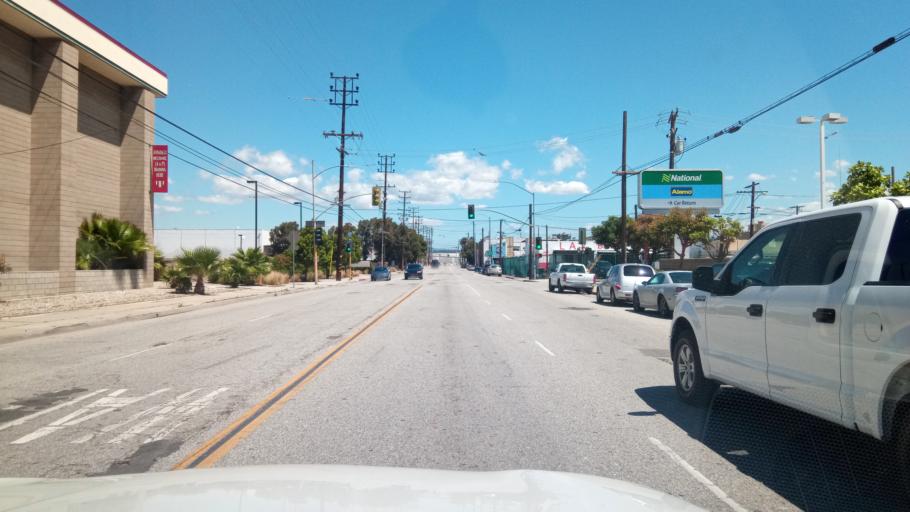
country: US
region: California
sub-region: Los Angeles County
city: Inglewood
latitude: 33.9558
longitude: -118.3770
